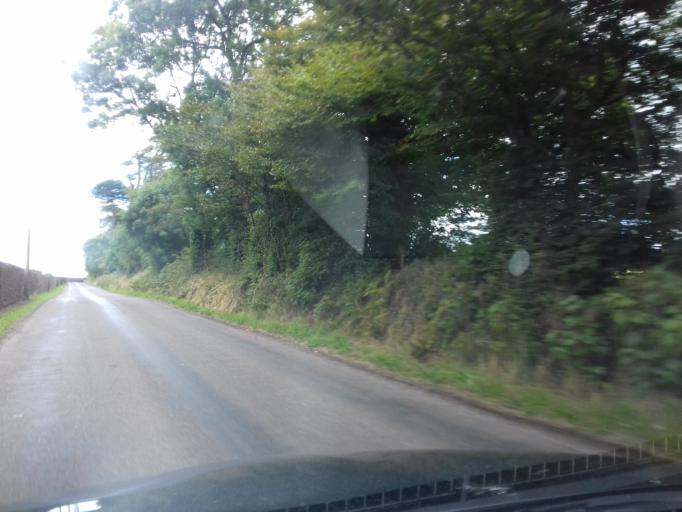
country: IE
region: Munster
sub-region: Waterford
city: Portlaw
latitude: 52.1777
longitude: -7.3468
